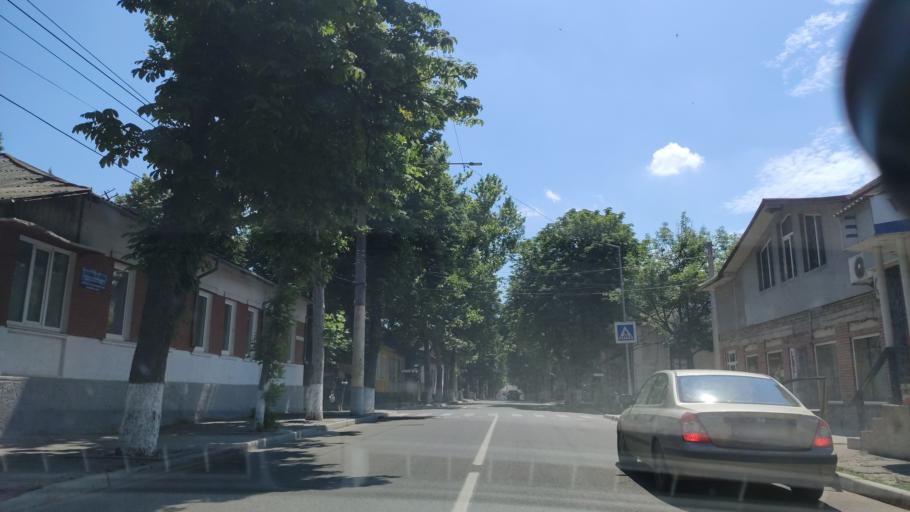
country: MD
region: Raionul Soroca
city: Soroca
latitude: 48.1519
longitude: 28.3002
